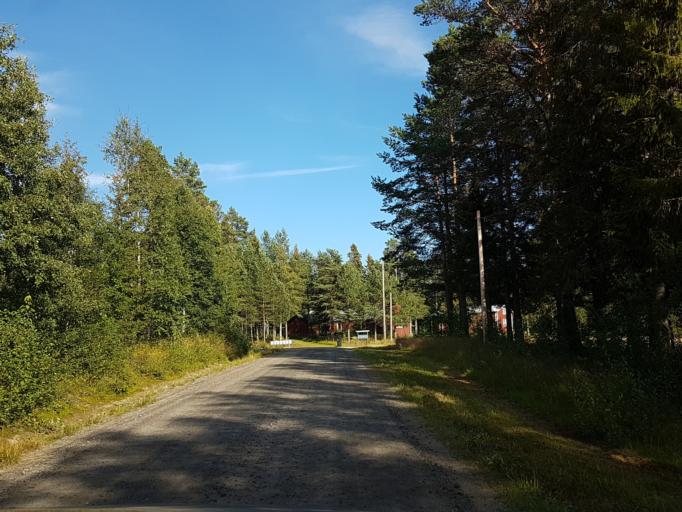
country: SE
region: Vaesterbotten
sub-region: Robertsfors Kommun
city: Robertsfors
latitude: 64.0490
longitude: 20.8836
